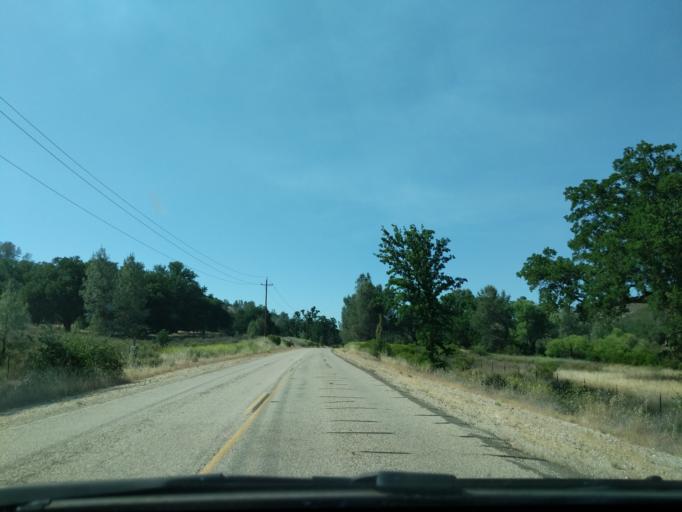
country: US
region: California
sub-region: Monterey County
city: King City
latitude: 35.9804
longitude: -121.1773
